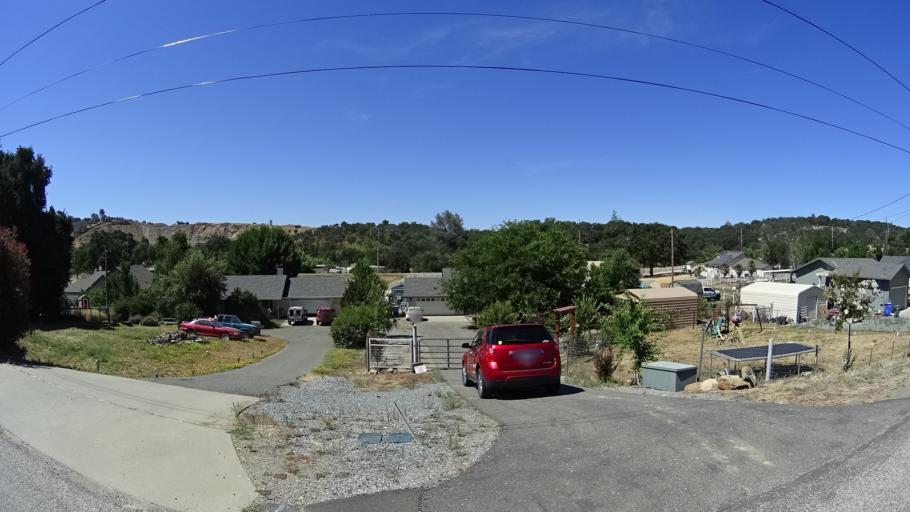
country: US
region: California
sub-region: Calaveras County
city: Rancho Calaveras
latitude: 38.1529
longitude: -120.8312
